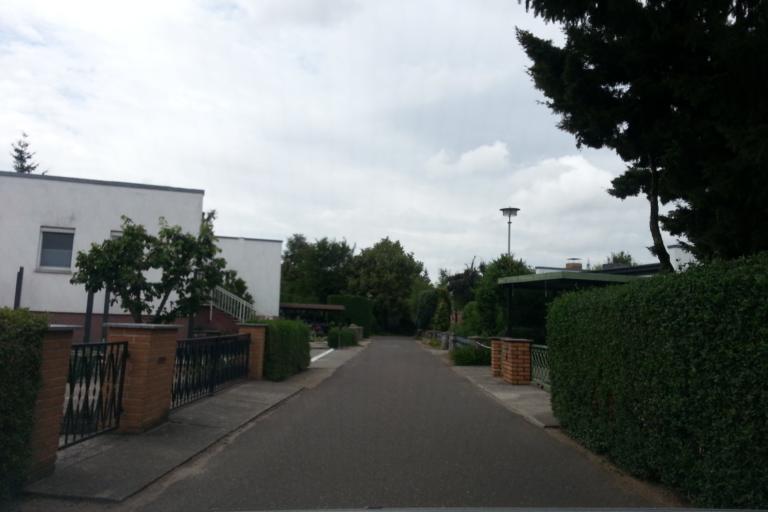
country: DE
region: Mecklenburg-Vorpommern
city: Ferdinandshof
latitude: 53.6605
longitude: 13.8961
